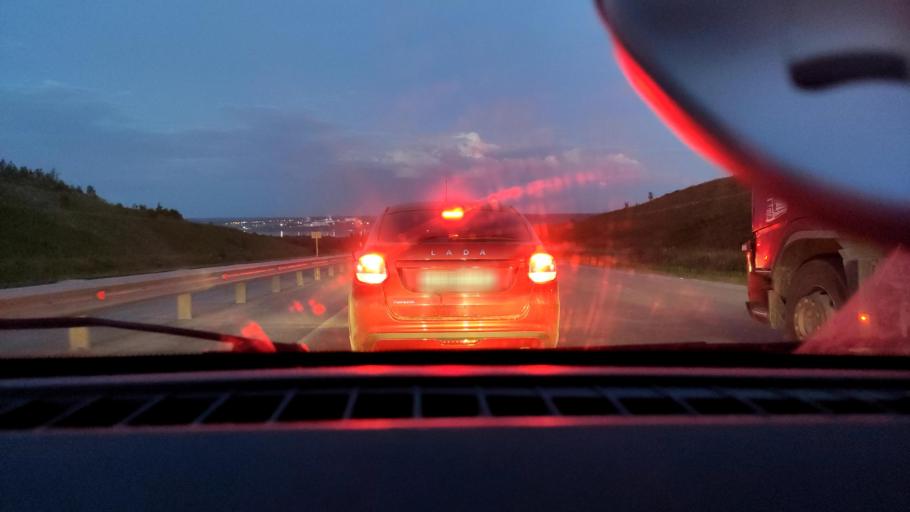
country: RU
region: Perm
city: Polazna
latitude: 58.1913
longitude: 56.4090
